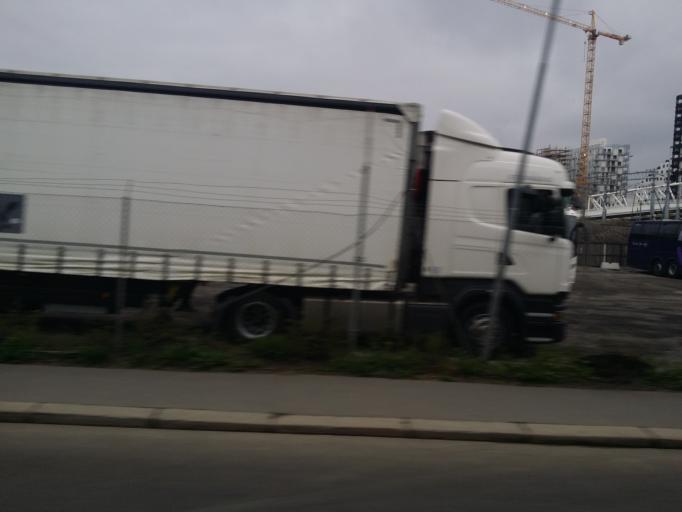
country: NO
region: Oslo
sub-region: Oslo
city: Oslo
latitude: 59.9091
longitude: 10.7665
